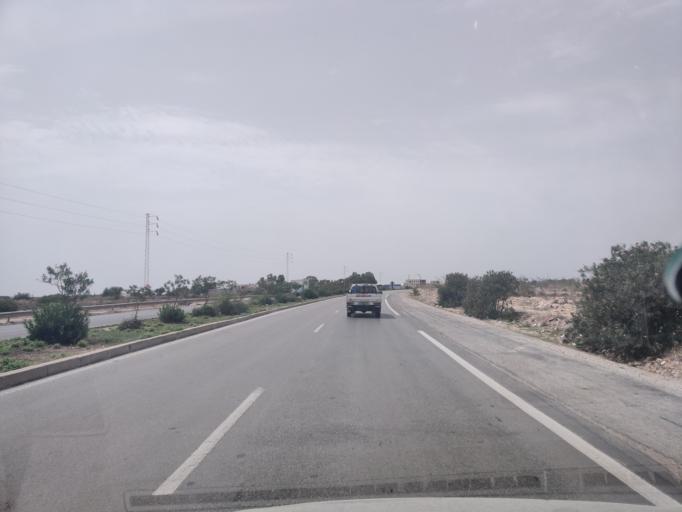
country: TN
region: Susah
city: Akouda
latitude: 35.8357
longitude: 10.5501
